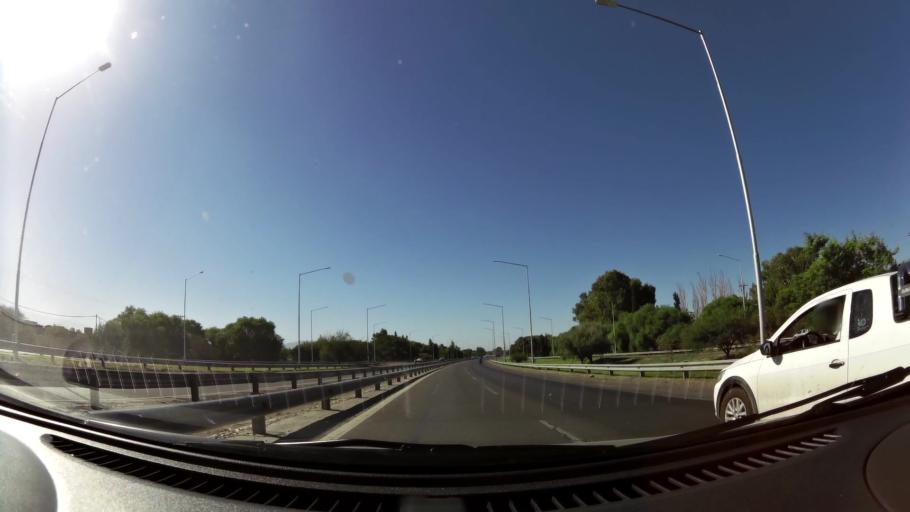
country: AR
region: San Juan
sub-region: Departamento de Santa Lucia
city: Santa Lucia
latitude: -31.5314
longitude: -68.5039
